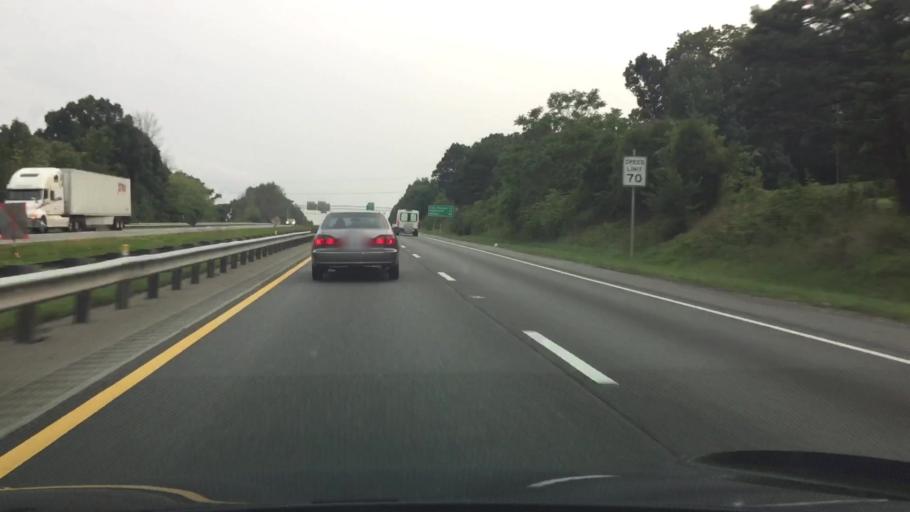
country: US
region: Virginia
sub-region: Pulaski County
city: Pulaski
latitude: 37.0201
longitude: -80.7353
